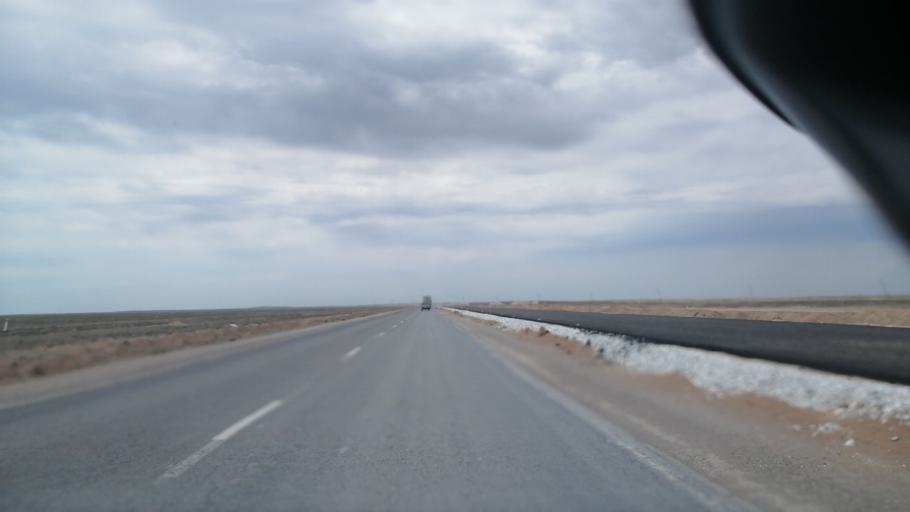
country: KZ
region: Qaraghandy
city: Saryshaghan
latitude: 46.5301
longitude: 74.1410
